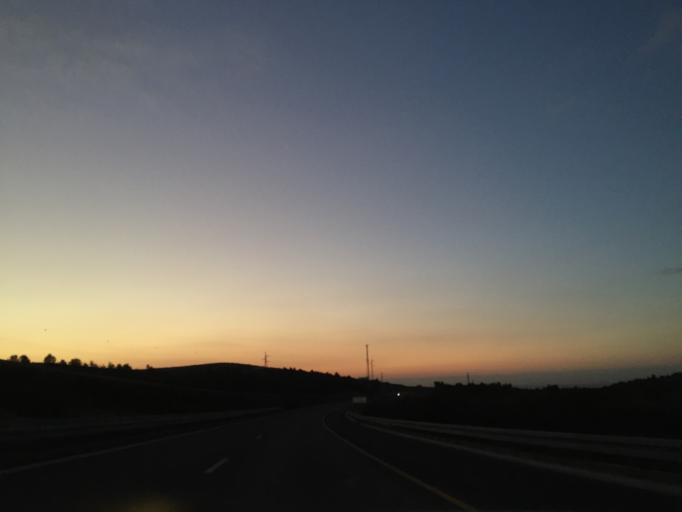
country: IL
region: Southern District
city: Lehavim
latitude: 31.3673
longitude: 34.8368
